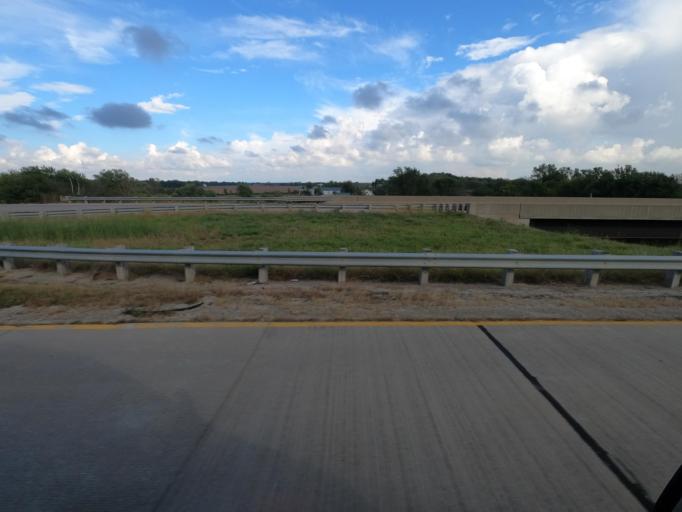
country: US
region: Illinois
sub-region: Hancock County
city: Nauvoo
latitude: 40.5324
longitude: -91.5632
